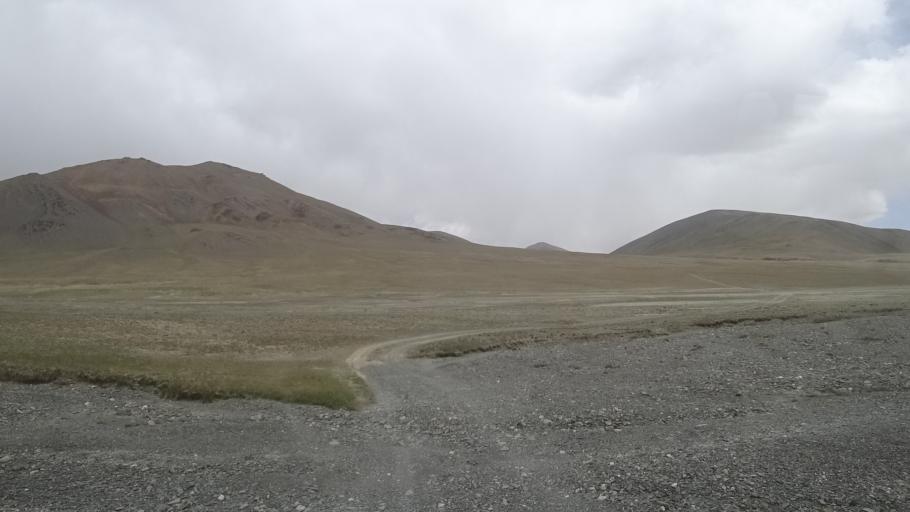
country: TJ
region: Gorno-Badakhshan
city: Murghob
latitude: 37.4921
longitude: 74.0314
